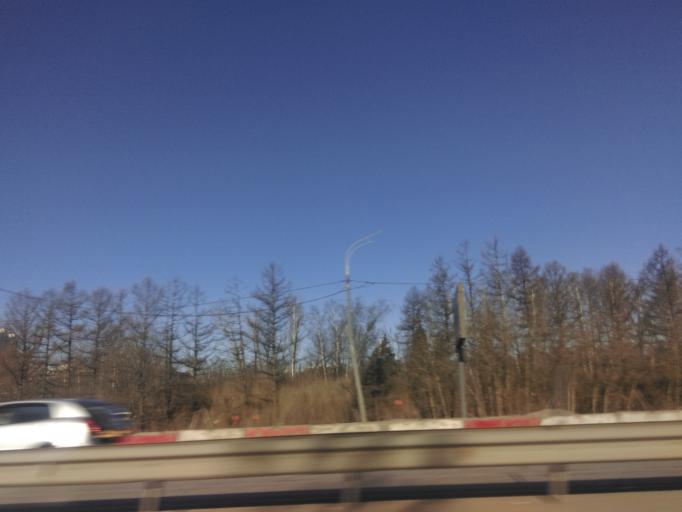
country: RU
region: Moskovskaya
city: Novoivanovskoye
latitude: 55.6957
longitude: 37.3398
